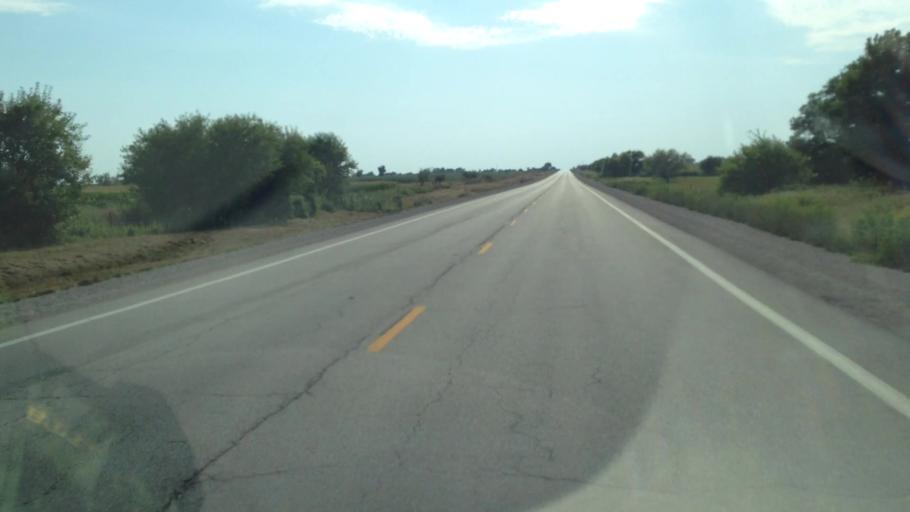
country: US
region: Kansas
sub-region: Anderson County
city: Garnett
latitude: 38.0816
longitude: -95.1953
